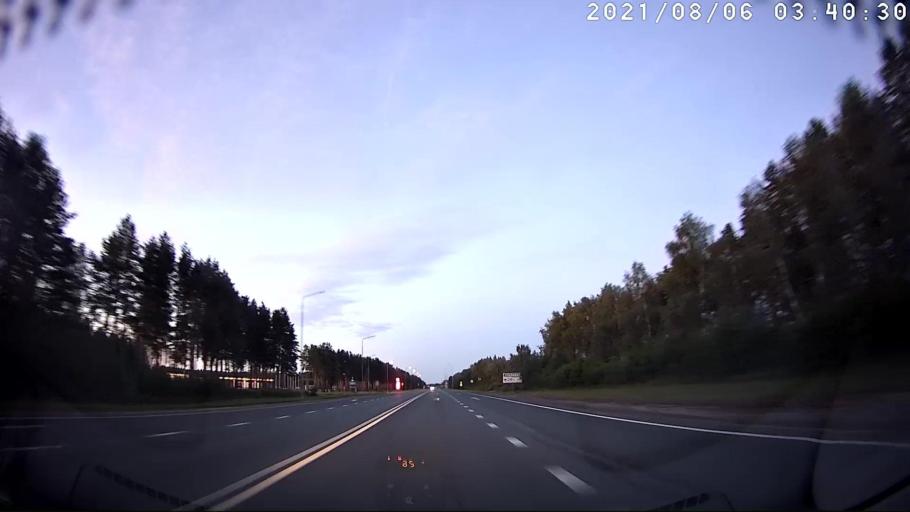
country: RU
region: Mariy-El
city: Pomary
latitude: 55.9458
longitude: 48.3692
